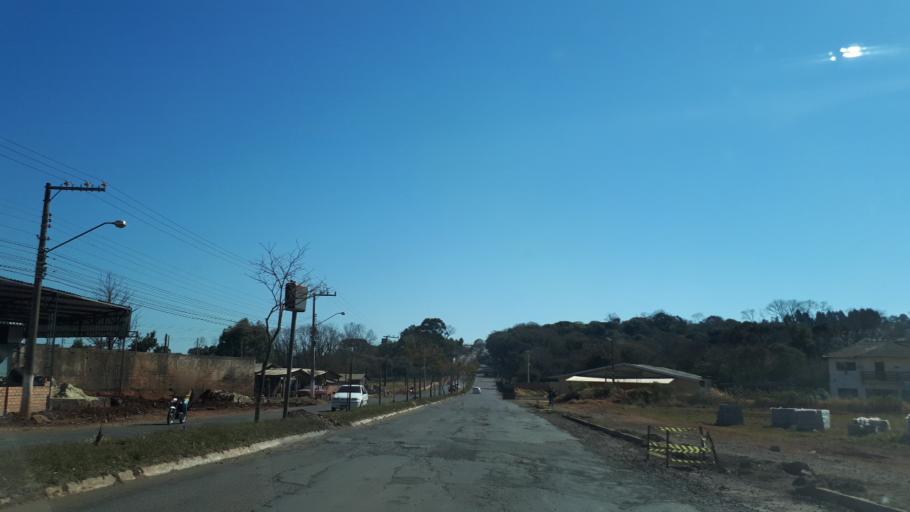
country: BR
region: Santa Catarina
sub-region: Chapeco
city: Chapeco
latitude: -27.1311
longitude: -52.6027
